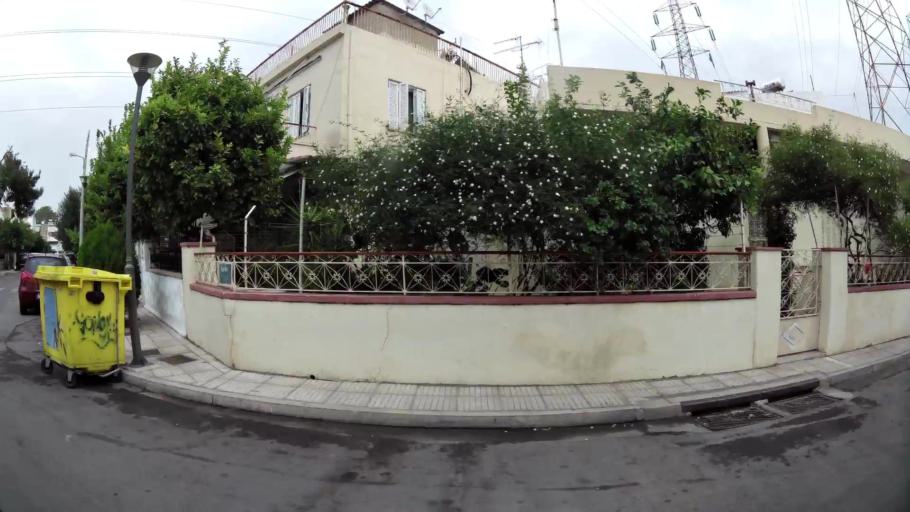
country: GR
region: Attica
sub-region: Nomarchia Athinas
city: Aigaleo
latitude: 37.9835
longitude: 23.6762
